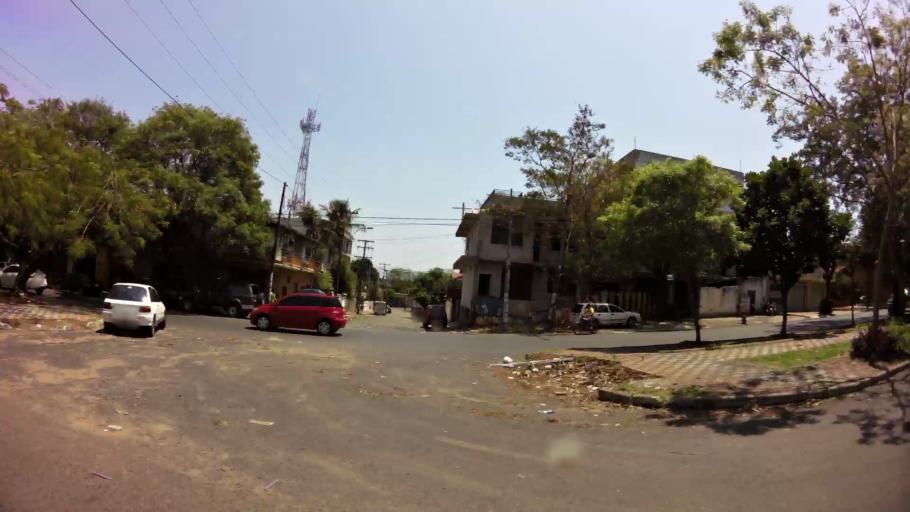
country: PY
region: Asuncion
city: Asuncion
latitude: -25.2998
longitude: -57.6350
